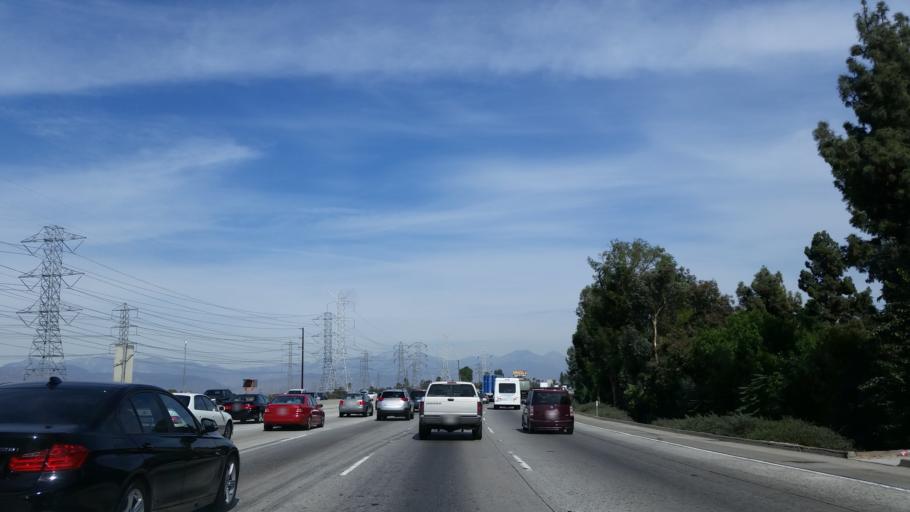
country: US
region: California
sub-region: Los Angeles County
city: South El Monte
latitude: 34.0380
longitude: -118.0217
